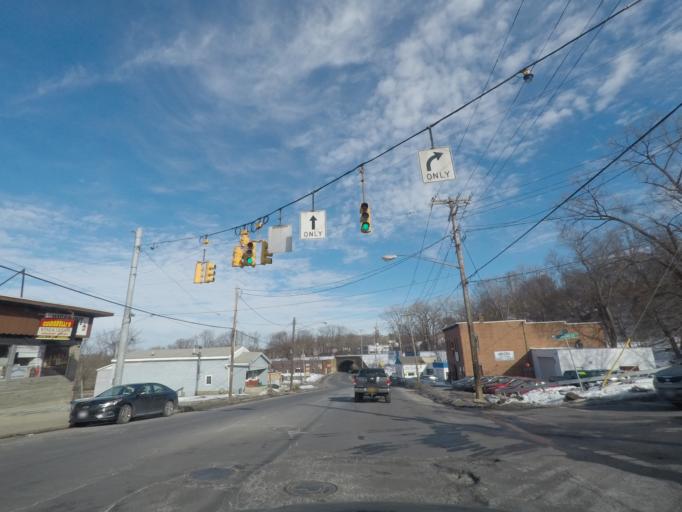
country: US
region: New York
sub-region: Schenectady County
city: Schenectady
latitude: 42.8027
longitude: -73.9563
